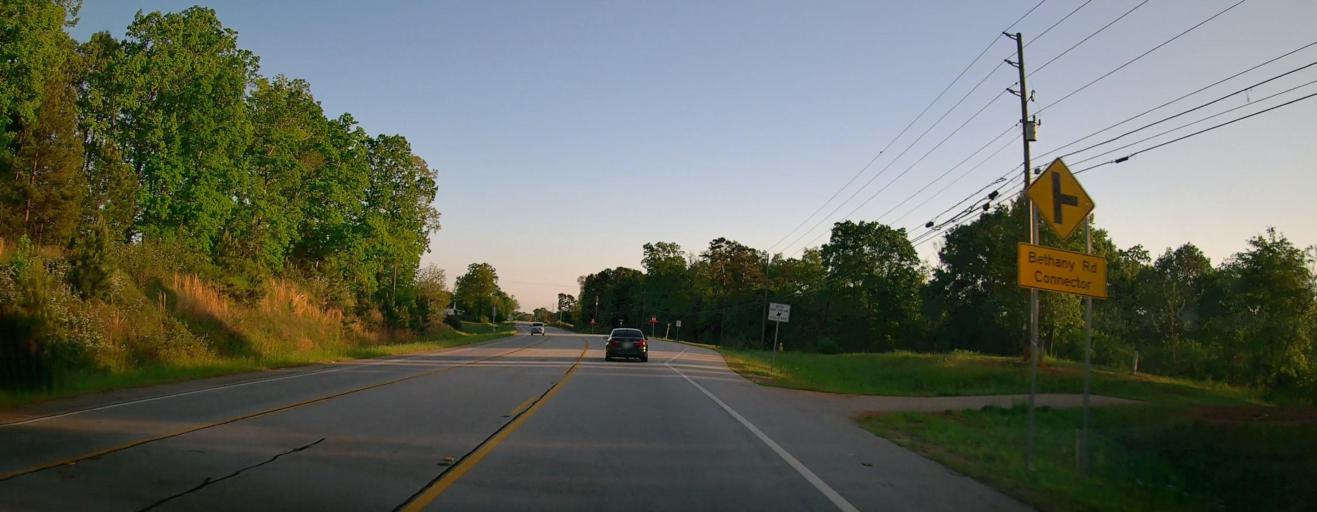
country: US
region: Georgia
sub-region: Newton County
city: Oakwood
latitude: 33.5372
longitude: -83.9520
